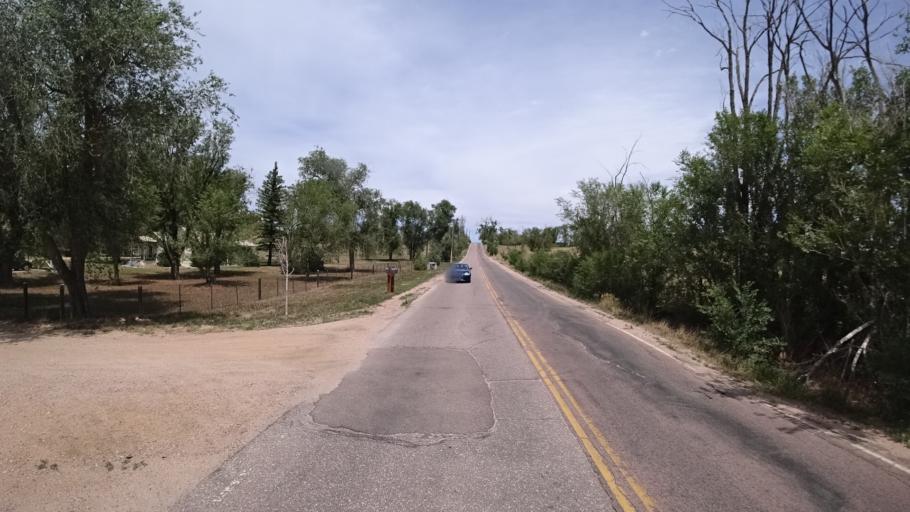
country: US
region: Colorado
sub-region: El Paso County
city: Fountain
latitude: 38.6792
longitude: -104.6736
